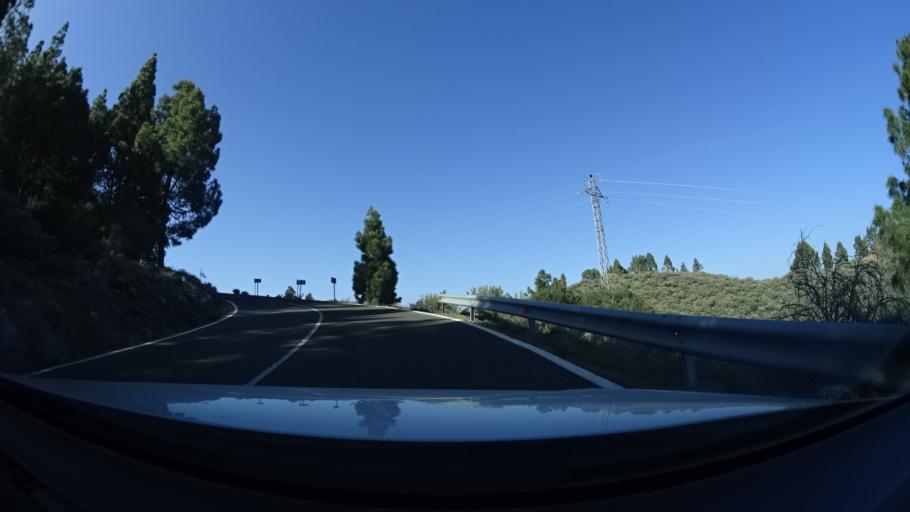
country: ES
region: Canary Islands
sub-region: Provincia de Las Palmas
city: Vega de San Mateo
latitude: 27.9645
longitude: -15.5397
